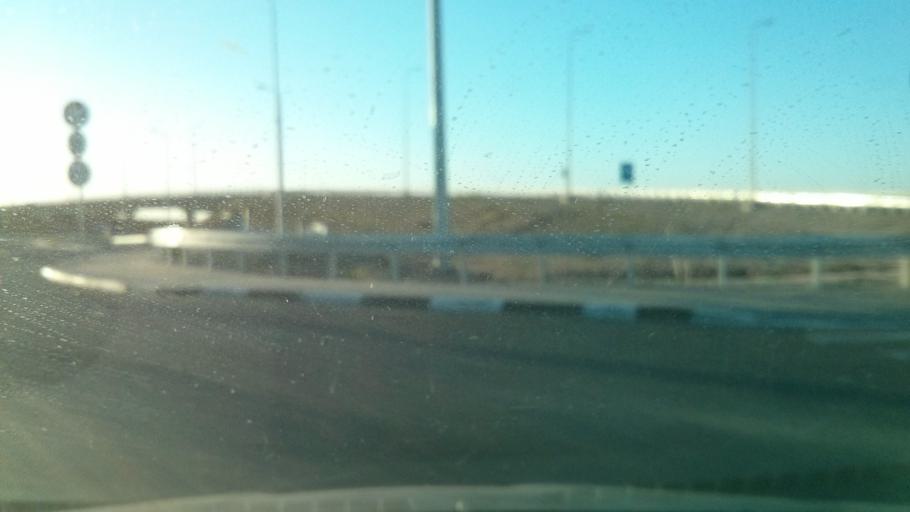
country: IL
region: Southern District
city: Lehavim
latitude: 31.4231
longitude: 34.7869
